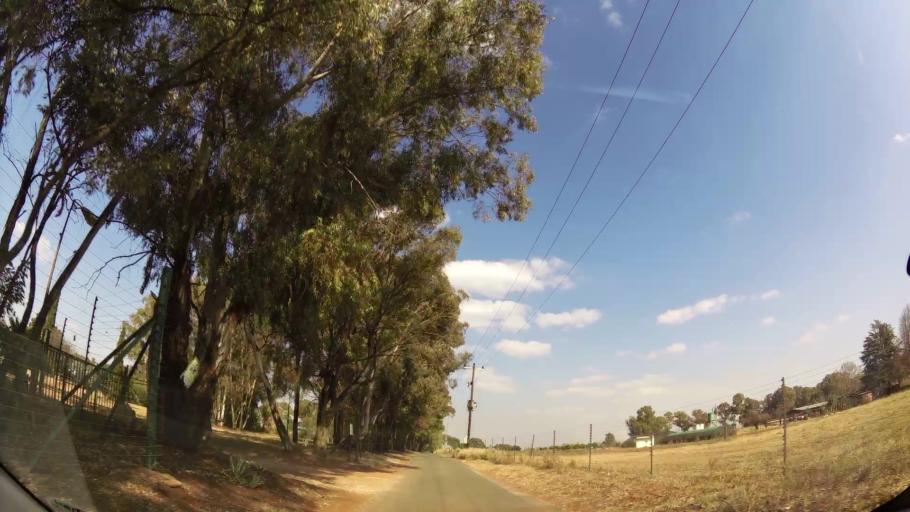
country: ZA
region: Gauteng
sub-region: Ekurhuleni Metropolitan Municipality
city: Benoni
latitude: -26.0851
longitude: 28.3586
